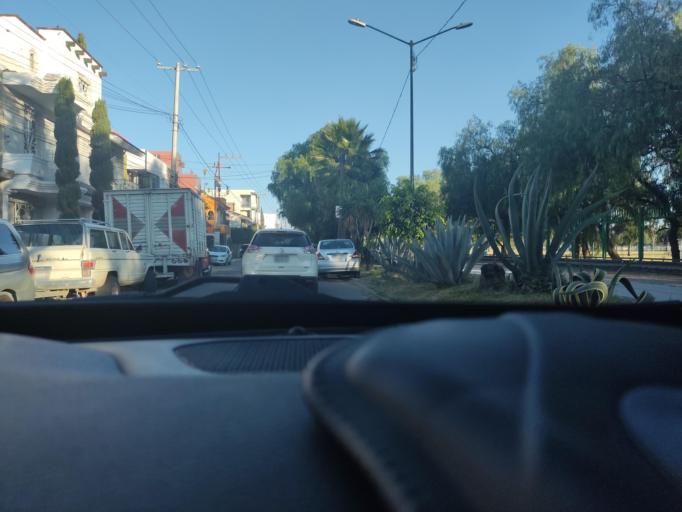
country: MX
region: Guanajuato
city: Leon
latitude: 21.1096
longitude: -101.6348
